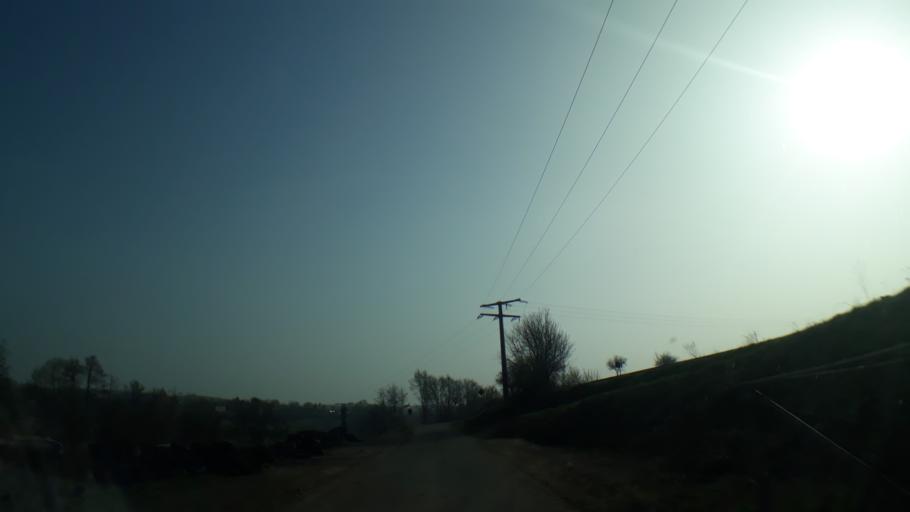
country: DE
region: North Rhine-Westphalia
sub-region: Regierungsbezirk Koln
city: Bad Munstereifel
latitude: 50.5558
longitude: 6.7202
